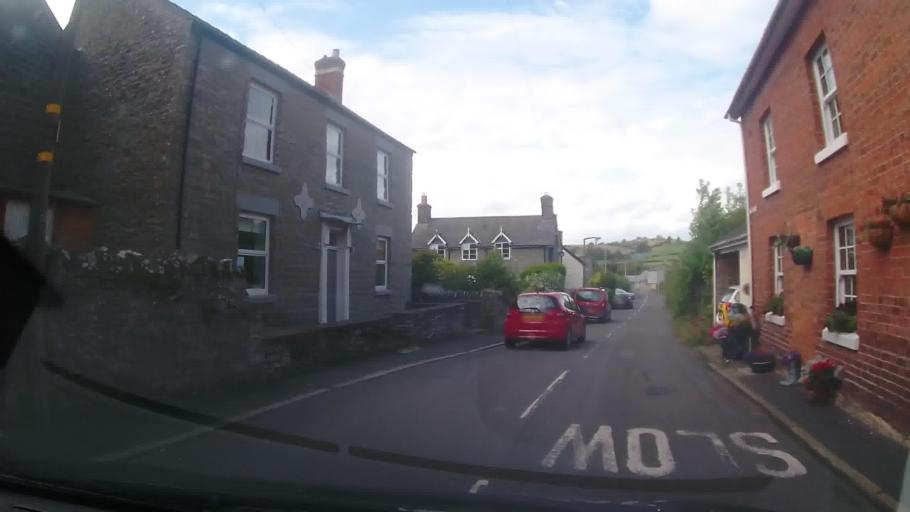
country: GB
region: England
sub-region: Shropshire
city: Acton
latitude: 52.4233
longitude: -3.0315
